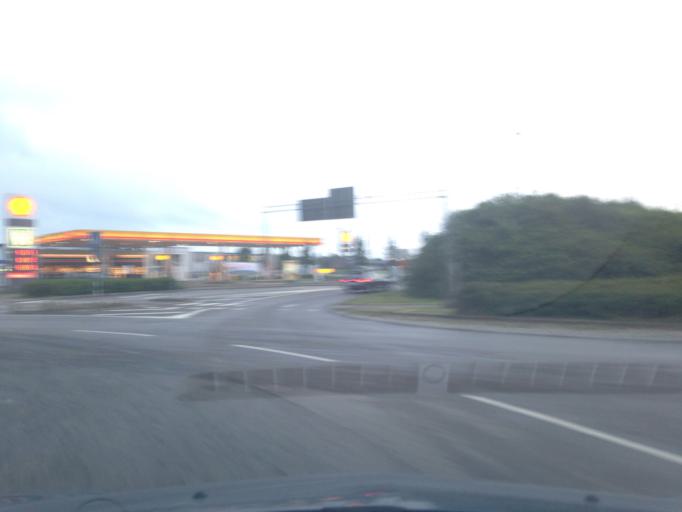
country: SE
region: Halland
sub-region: Varbergs Kommun
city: Varberg
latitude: 57.1235
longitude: 12.2619
